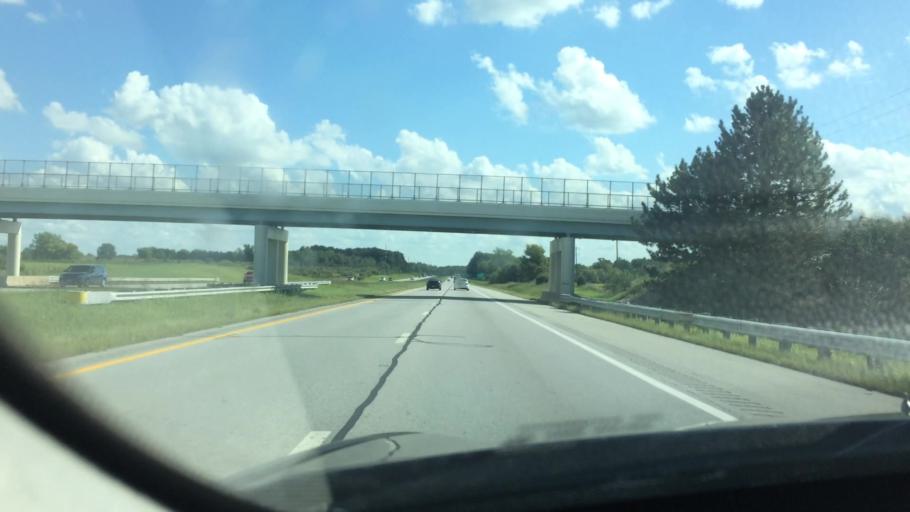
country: US
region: Ohio
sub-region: Shelby County
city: Anna
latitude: 40.3467
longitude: -84.1600
